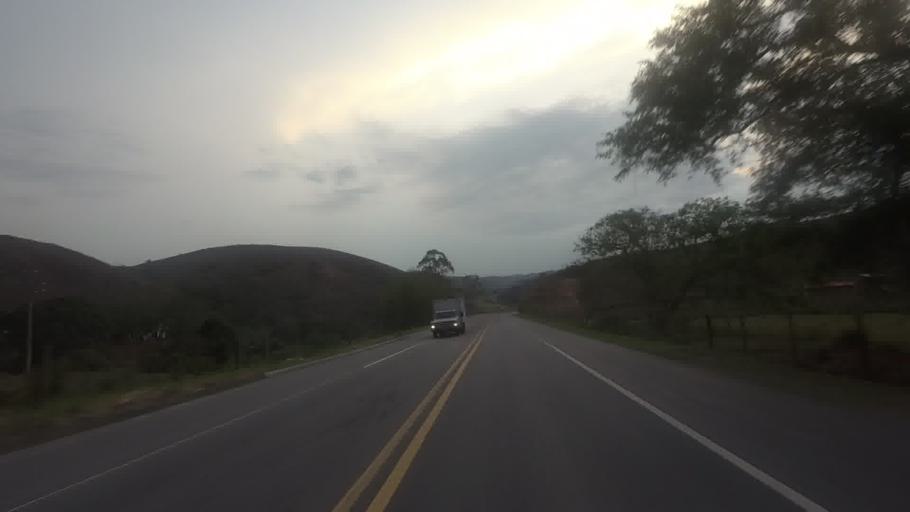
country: BR
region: Minas Gerais
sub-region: Alem Paraiba
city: Alem Paraiba
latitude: -21.8461
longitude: -42.6330
